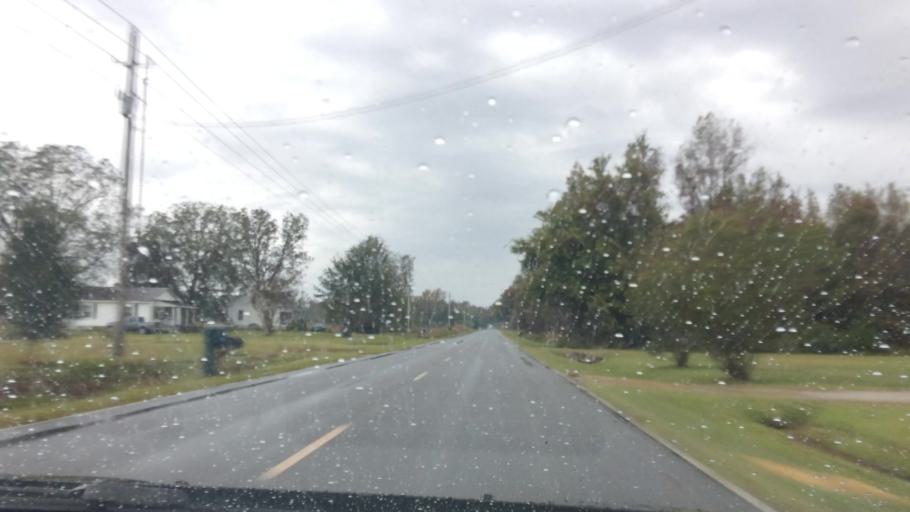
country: US
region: North Carolina
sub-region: Pitt County
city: Grifton
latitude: 35.4023
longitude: -77.4138
